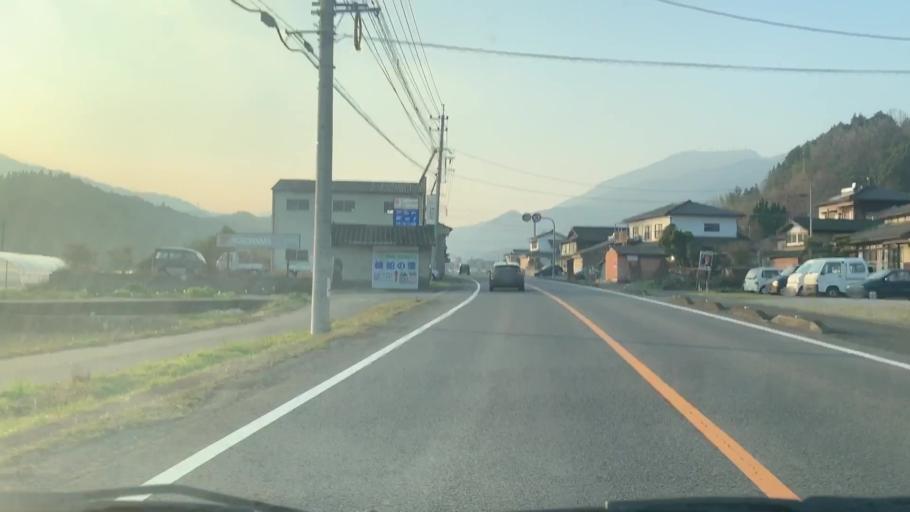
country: JP
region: Saga Prefecture
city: Takeocho-takeo
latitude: 33.2591
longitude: 130.0668
